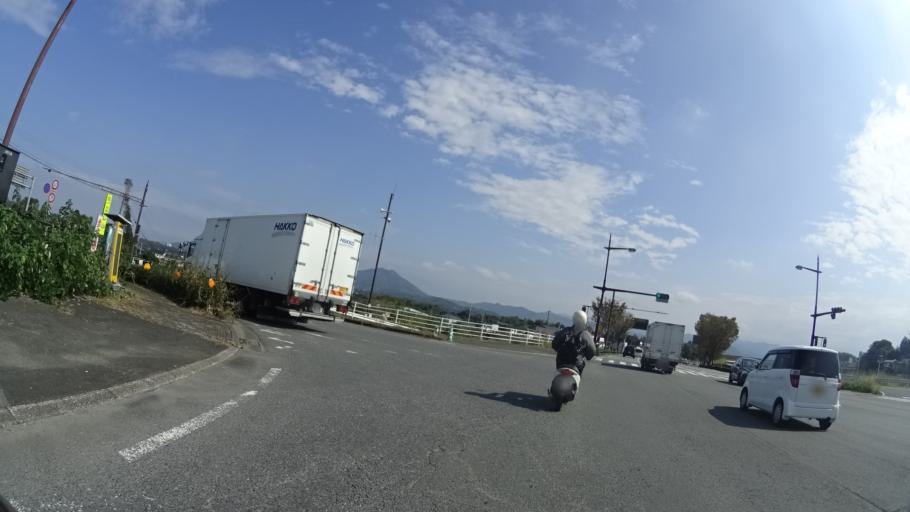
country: JP
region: Kumamoto
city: Kumamoto
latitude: 32.7336
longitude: 130.7719
